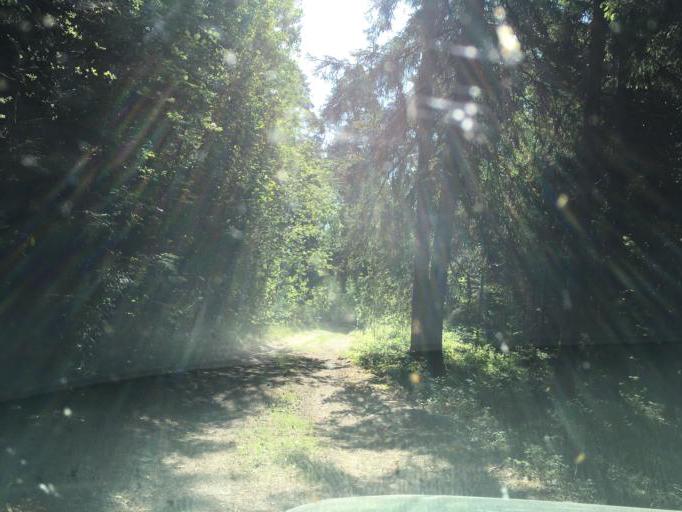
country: LV
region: Ventspils
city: Ventspils
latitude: 57.4718
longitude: 21.7691
